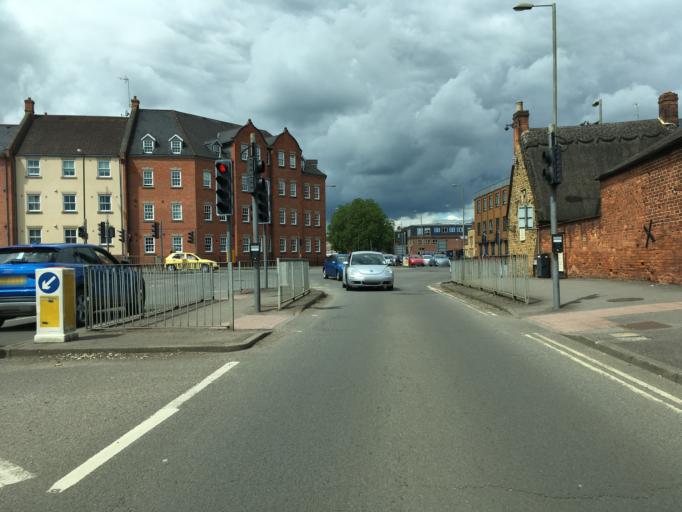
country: GB
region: England
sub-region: Oxfordshire
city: Banbury
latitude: 52.0635
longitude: -1.3392
